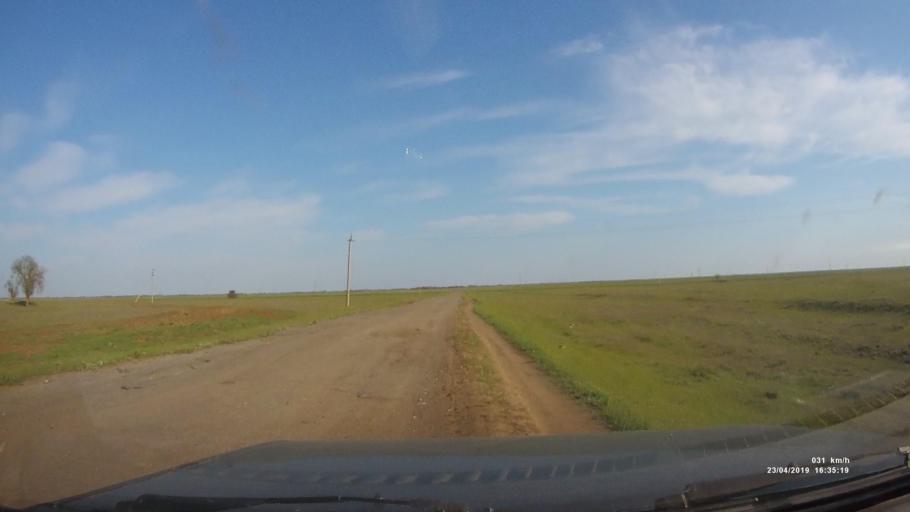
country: RU
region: Kalmykiya
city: Priyutnoye
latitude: 46.3314
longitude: 43.1369
